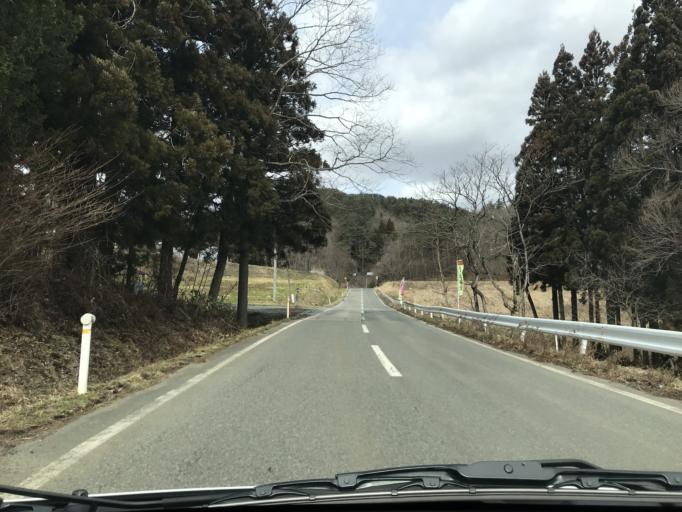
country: JP
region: Iwate
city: Kitakami
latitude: 39.2807
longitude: 141.3194
